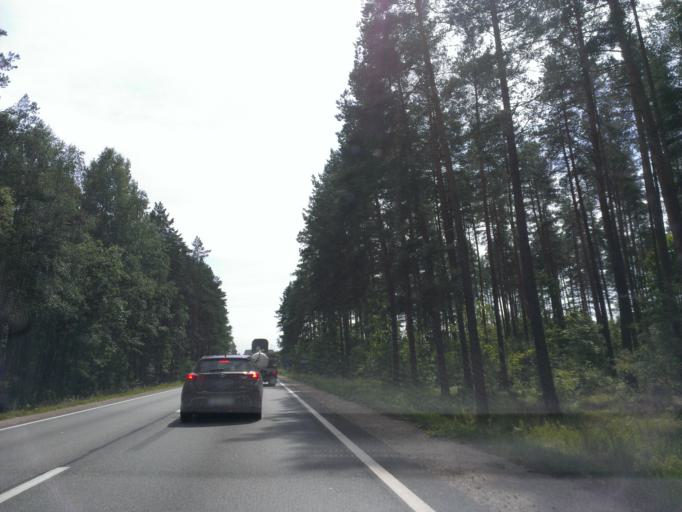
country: LV
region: Salaspils
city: Salaspils
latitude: 56.9464
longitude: 24.3805
